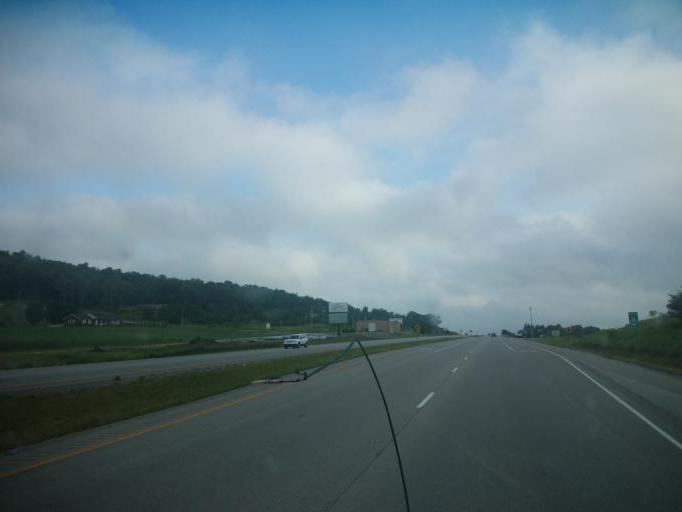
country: US
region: Kentucky
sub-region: Clinton County
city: Albany
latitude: 36.7391
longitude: -85.1341
